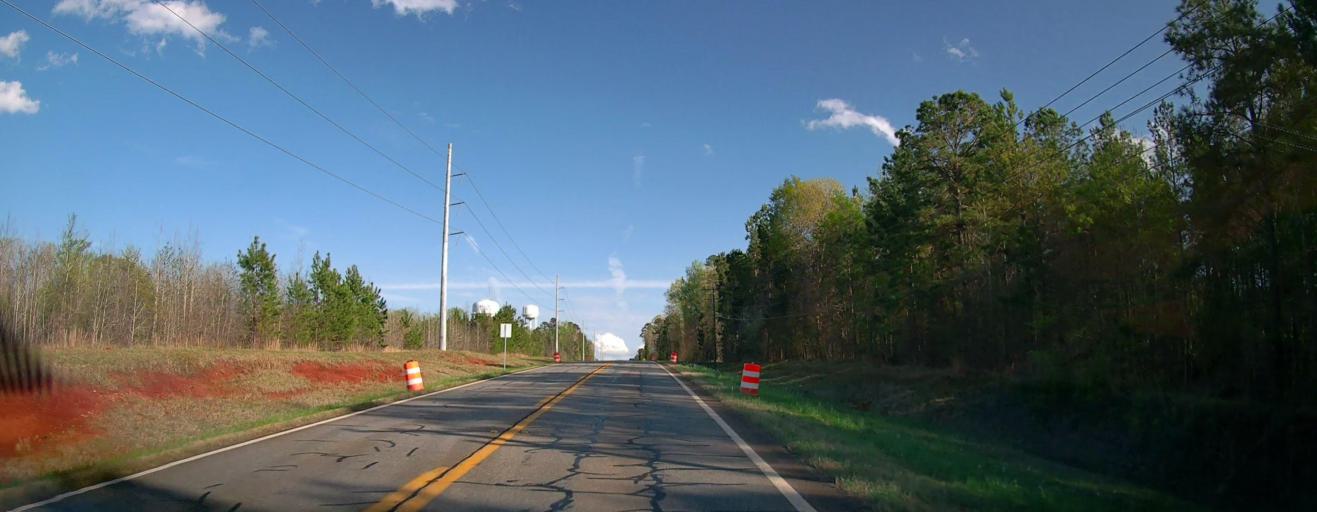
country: US
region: Georgia
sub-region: Baldwin County
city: Milledgeville
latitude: 33.1447
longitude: -83.3362
